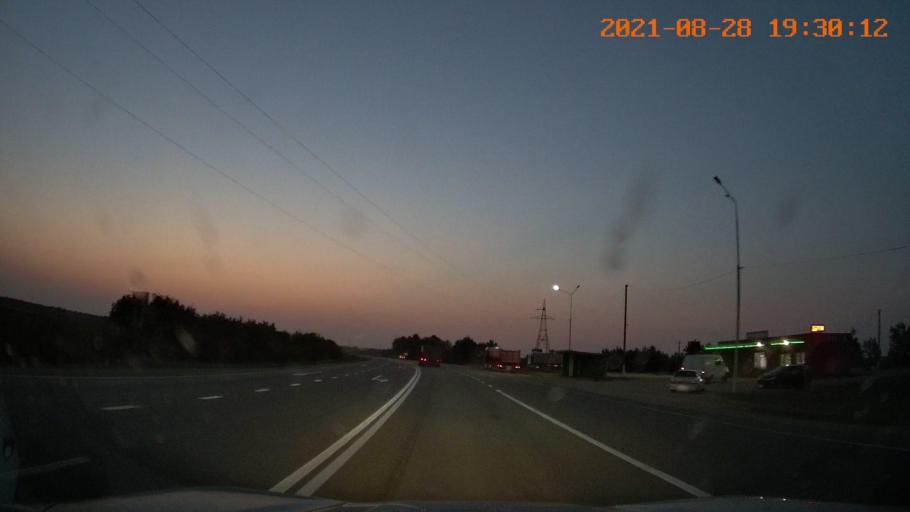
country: RU
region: Adygeya
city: Ponezhukay
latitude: 44.8954
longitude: 39.3552
